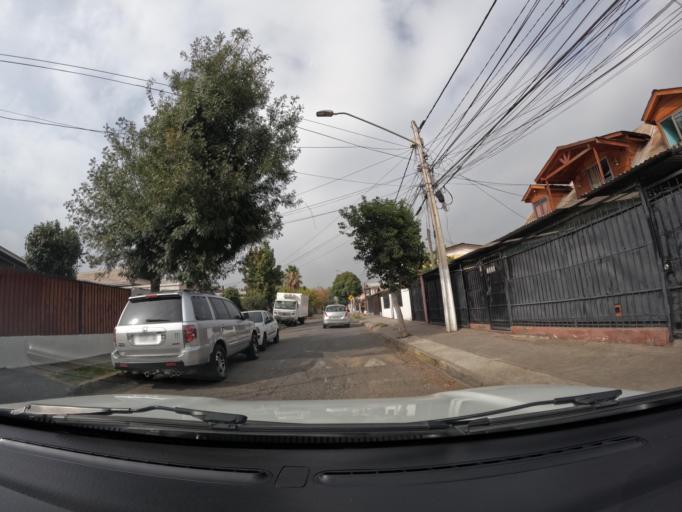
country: CL
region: Santiago Metropolitan
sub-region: Provincia de Santiago
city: Villa Presidente Frei, Nunoa, Santiago, Chile
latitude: -33.4715
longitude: -70.5477
